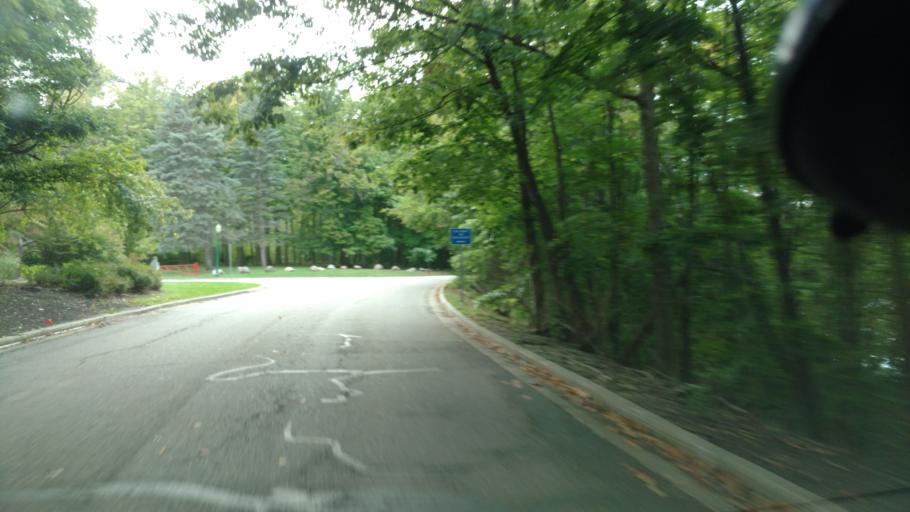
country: US
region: Michigan
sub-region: Ingham County
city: Edgemont Park
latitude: 42.7200
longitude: -84.5865
